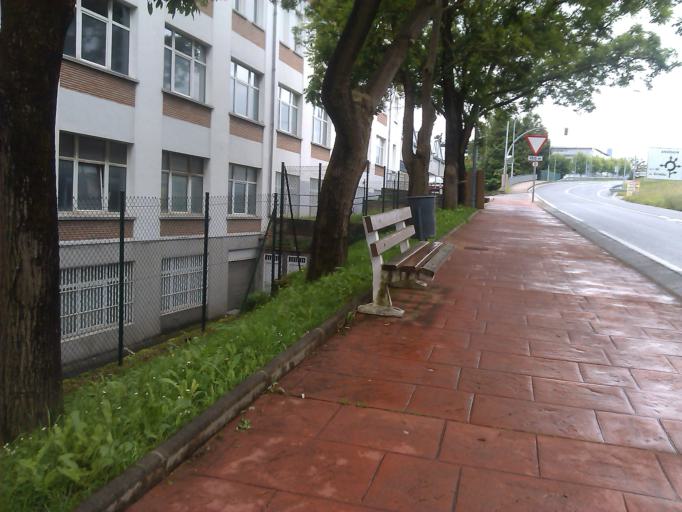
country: ES
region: Basque Country
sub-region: Provincia de Guipuzcoa
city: Urnieta
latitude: 43.2421
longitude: -1.9951
